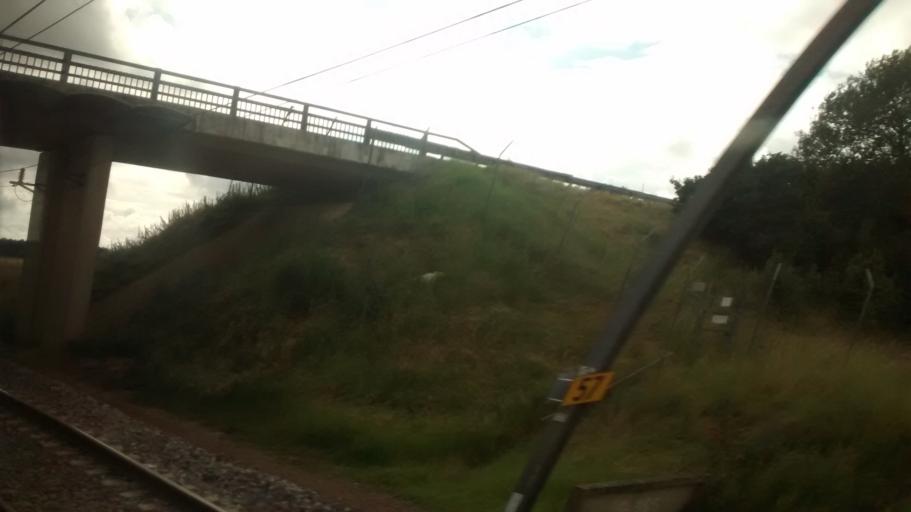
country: FR
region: Ile-de-France
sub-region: Departement des Yvelines
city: Ablis
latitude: 48.4793
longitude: 1.8635
